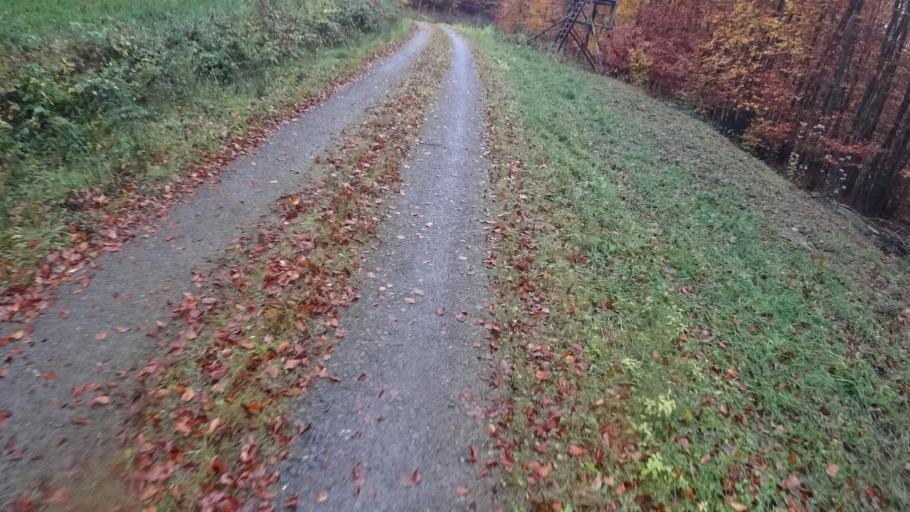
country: DE
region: Rheinland-Pfalz
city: Utzenhain
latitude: 50.1529
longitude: 7.6485
